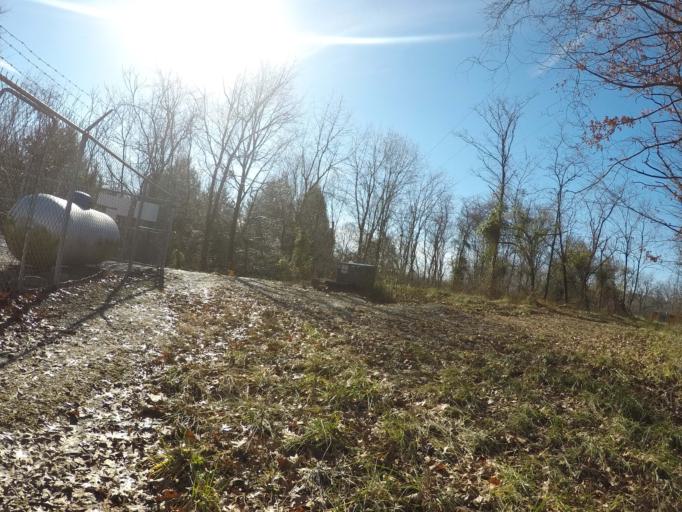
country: US
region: West Virginia
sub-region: Cabell County
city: Huntington
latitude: 38.4216
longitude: -82.3963
